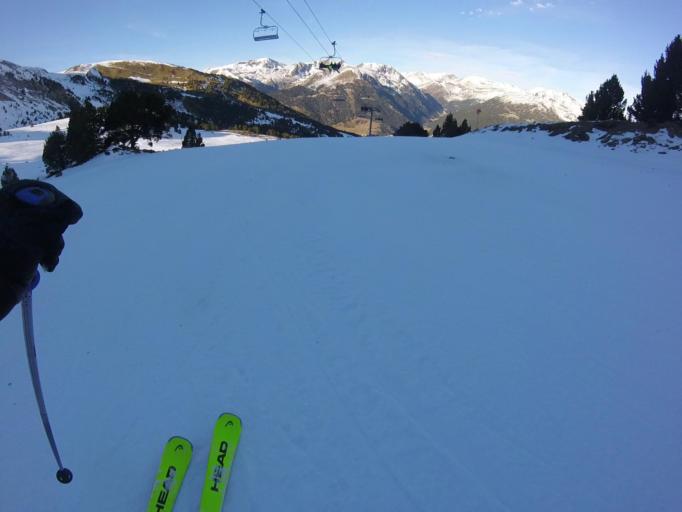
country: AD
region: Canillo
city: El Tarter
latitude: 42.5575
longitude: 1.6447
